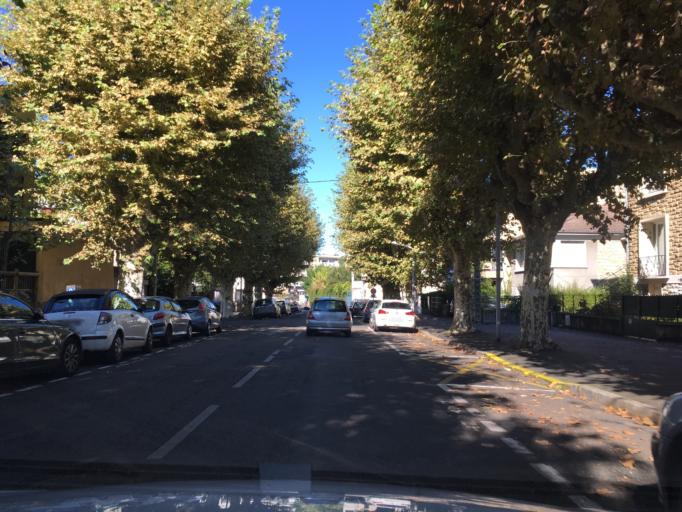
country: FR
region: Limousin
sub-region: Departement de la Correze
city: Brive-la-Gaillarde
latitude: 45.1608
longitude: 1.5304
